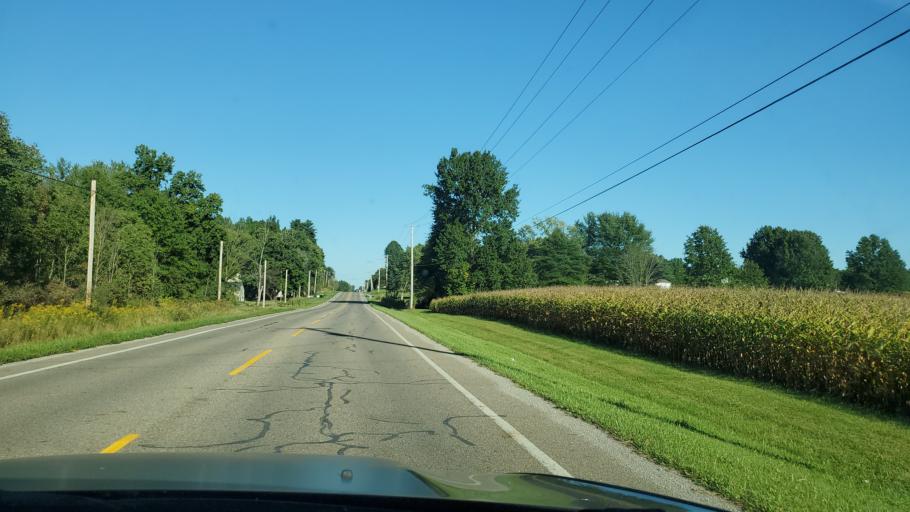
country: US
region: Ohio
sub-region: Mahoning County
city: Canfield
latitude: 40.9883
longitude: -80.7881
